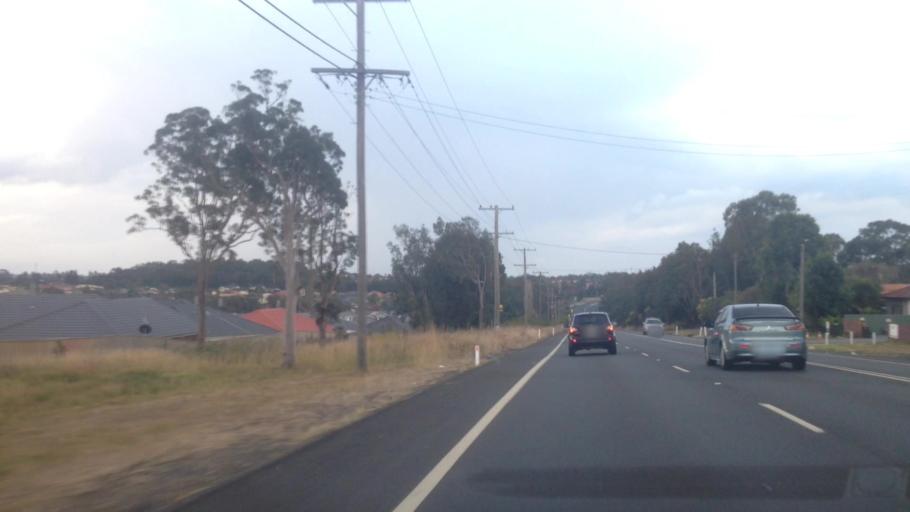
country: AU
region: New South Wales
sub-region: Wyong Shire
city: Kanwal
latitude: -33.2588
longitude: 151.4853
